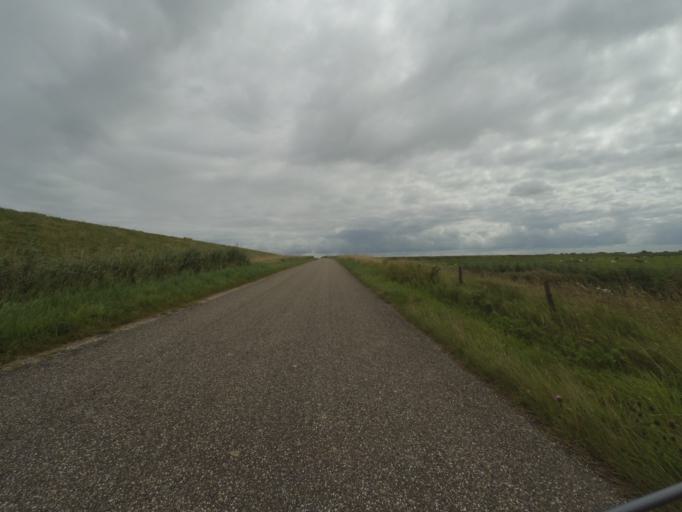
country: NL
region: Friesland
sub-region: Gemeente Dongeradeel
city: Anjum
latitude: 53.3522
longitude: 6.1430
